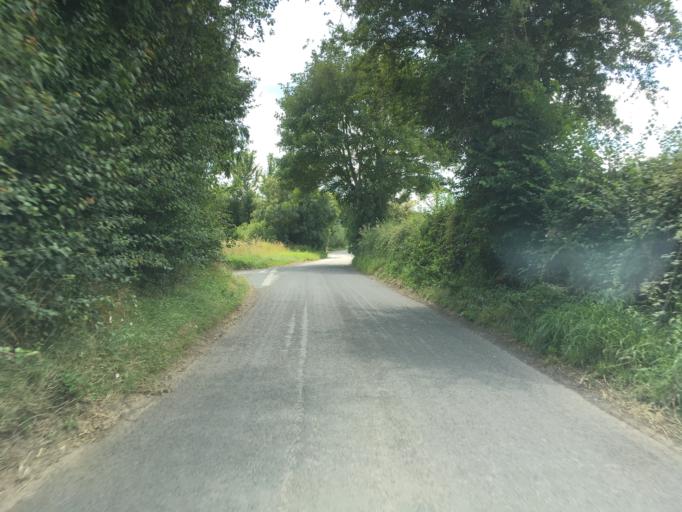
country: GB
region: England
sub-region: Gloucestershire
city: Gloucester
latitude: 51.8919
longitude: -2.2535
